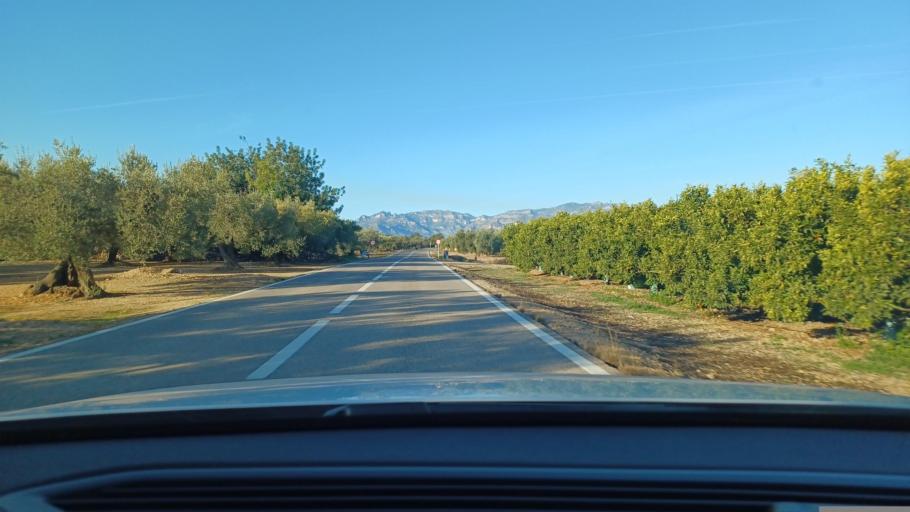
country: ES
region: Catalonia
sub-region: Provincia de Tarragona
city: Santa Barbara
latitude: 40.7198
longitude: 0.4597
